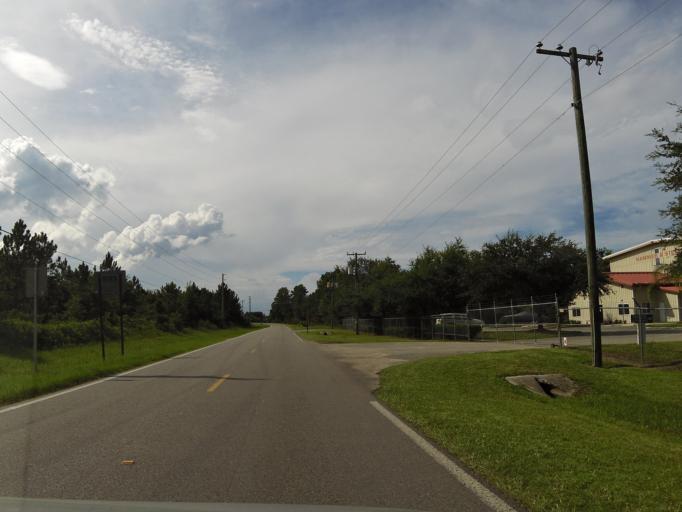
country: US
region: Florida
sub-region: Clay County
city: Green Cove Springs
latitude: 29.9588
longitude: -81.6692
